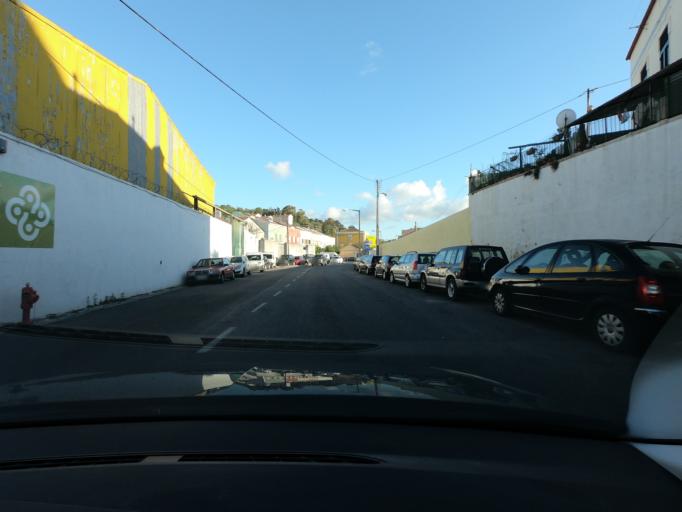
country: PT
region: Lisbon
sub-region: Lisbon
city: Lisbon
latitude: 38.7368
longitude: -9.1171
